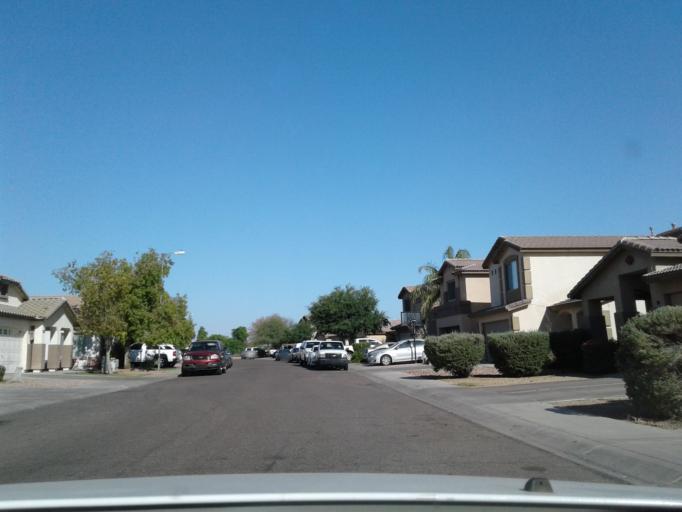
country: US
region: Arizona
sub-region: Maricopa County
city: Laveen
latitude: 33.4119
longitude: -112.1895
